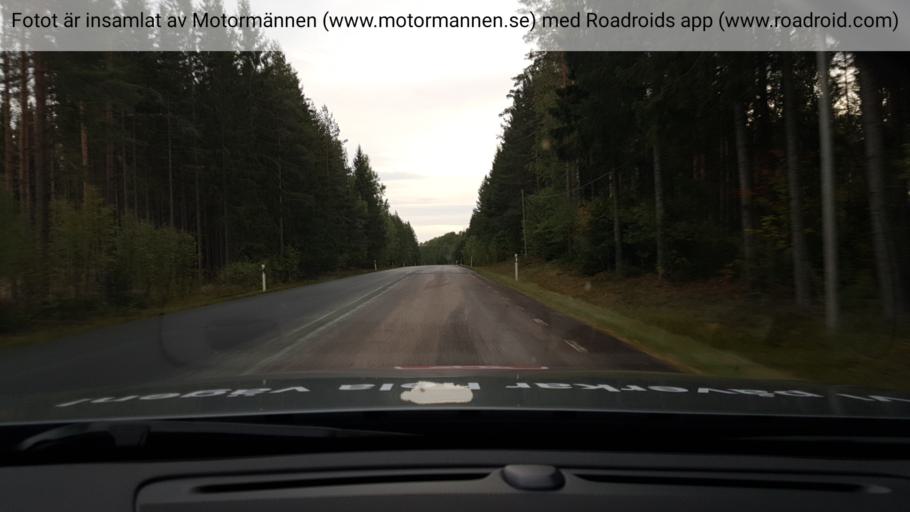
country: SE
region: Vaestra Goetaland
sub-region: Amals Kommun
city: Amal
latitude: 59.0655
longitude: 12.6533
